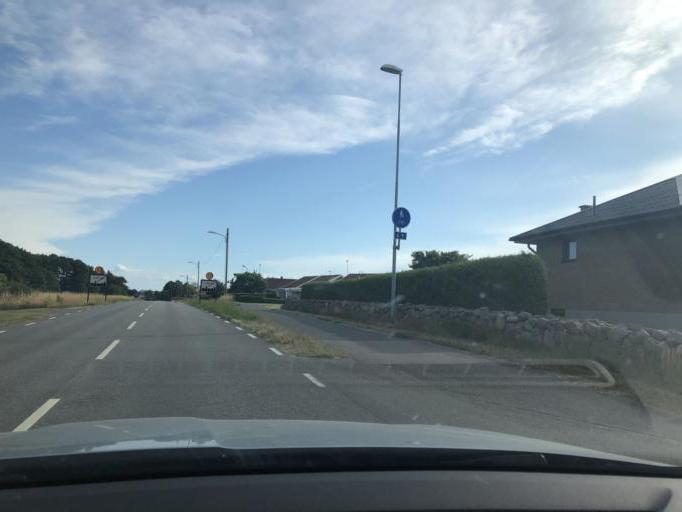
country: SE
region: Blekinge
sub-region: Solvesborgs Kommun
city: Soelvesborg
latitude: 56.0578
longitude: 14.5341
